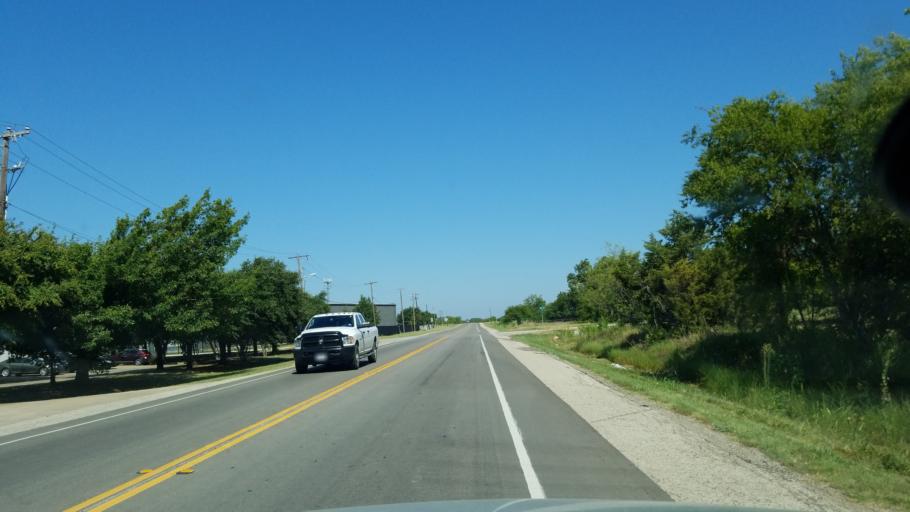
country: US
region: Texas
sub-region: Tarrant County
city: Mansfield
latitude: 32.5511
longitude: -97.1321
